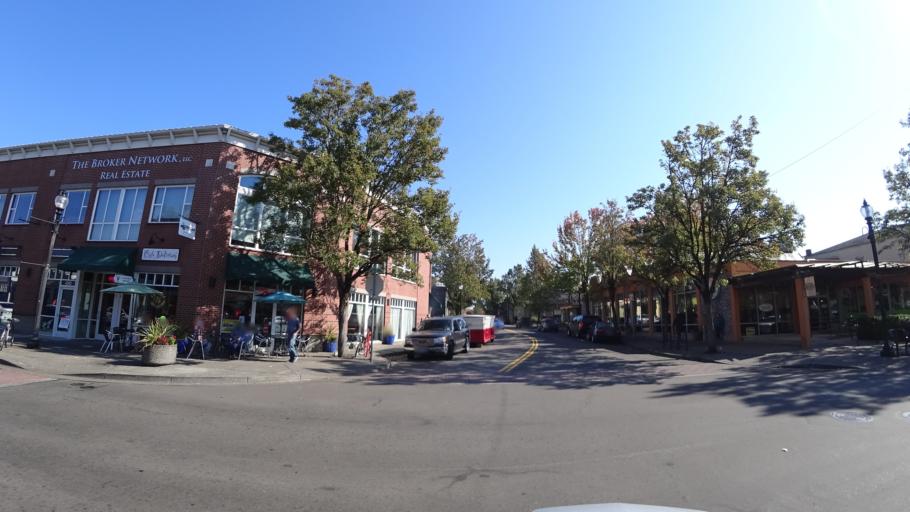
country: US
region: Oregon
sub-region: Multnomah County
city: Gresham
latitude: 45.4997
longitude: -122.4310
